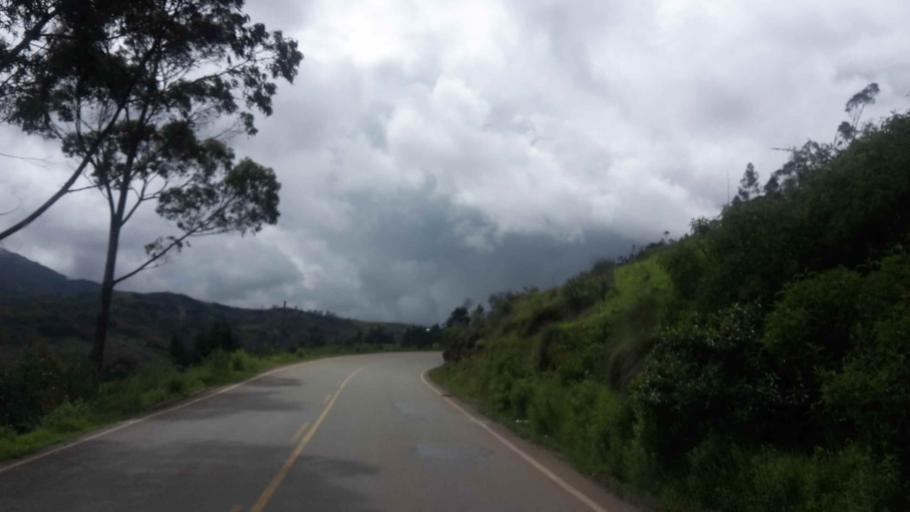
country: BO
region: Cochabamba
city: Totora
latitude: -17.5549
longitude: -65.3457
